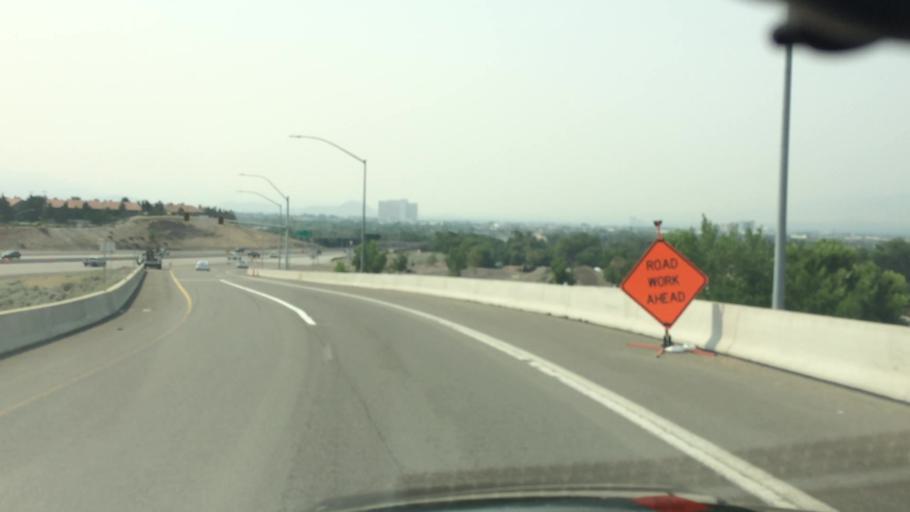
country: US
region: Nevada
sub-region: Washoe County
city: Reno
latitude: 39.5555
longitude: -119.7891
